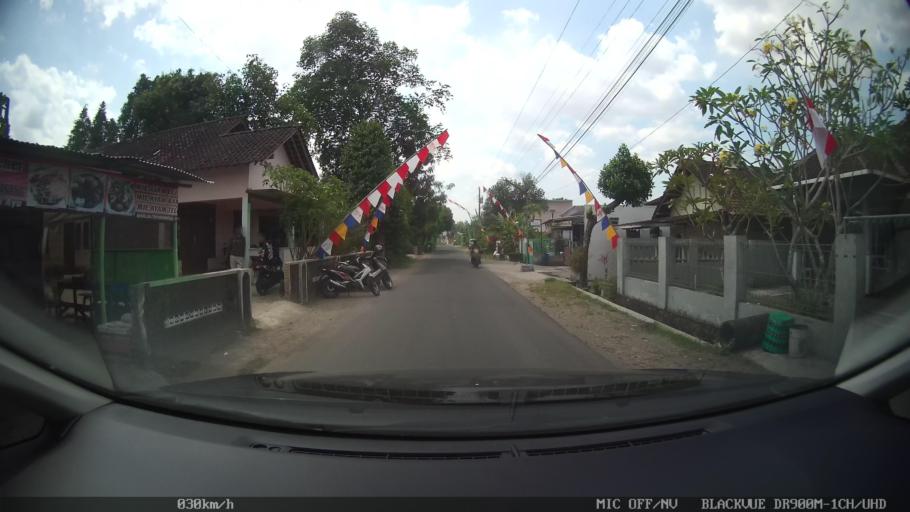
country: ID
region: Daerah Istimewa Yogyakarta
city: Kasihan
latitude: -7.8174
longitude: 110.3402
